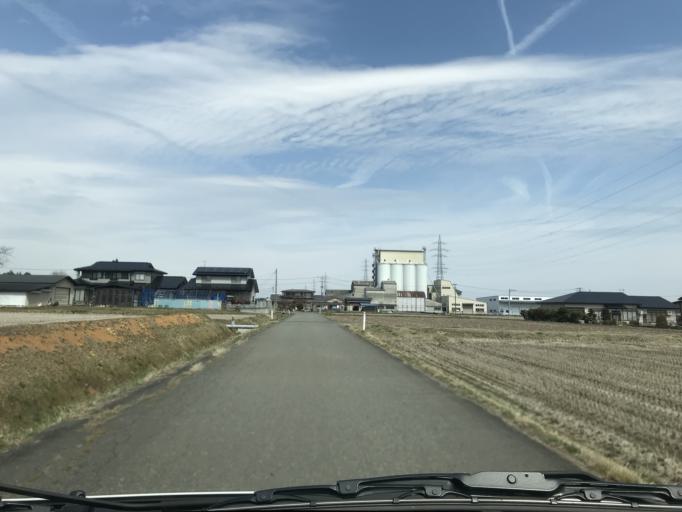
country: JP
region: Iwate
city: Mizusawa
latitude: 39.1380
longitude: 141.0832
